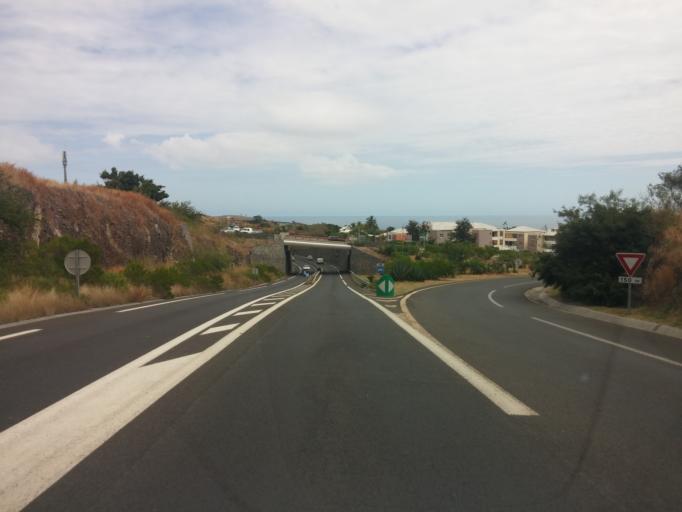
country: RE
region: Reunion
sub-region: Reunion
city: Saint-Paul
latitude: -21.0191
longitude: 55.2666
